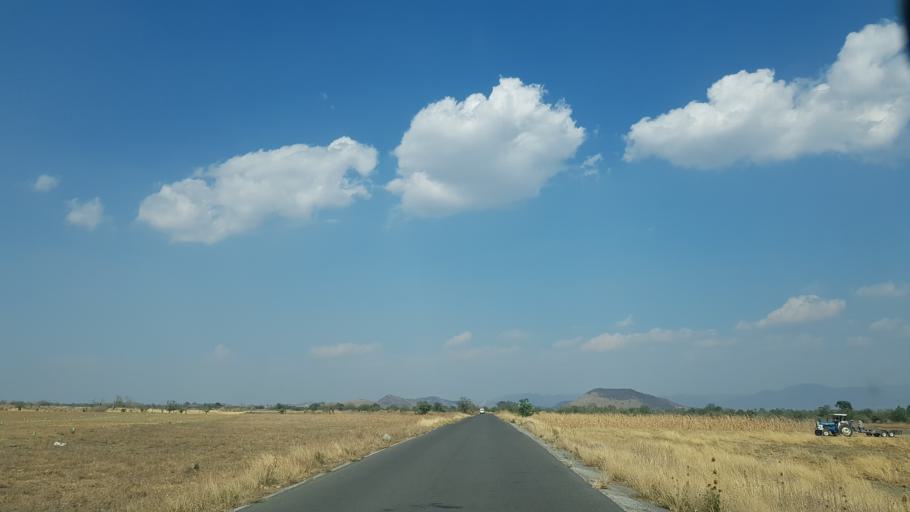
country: MX
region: Puebla
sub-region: Atlixco
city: Colonia Agricola de Ocotepec (Colonia San Jose)
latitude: 18.9219
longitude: -98.5124
